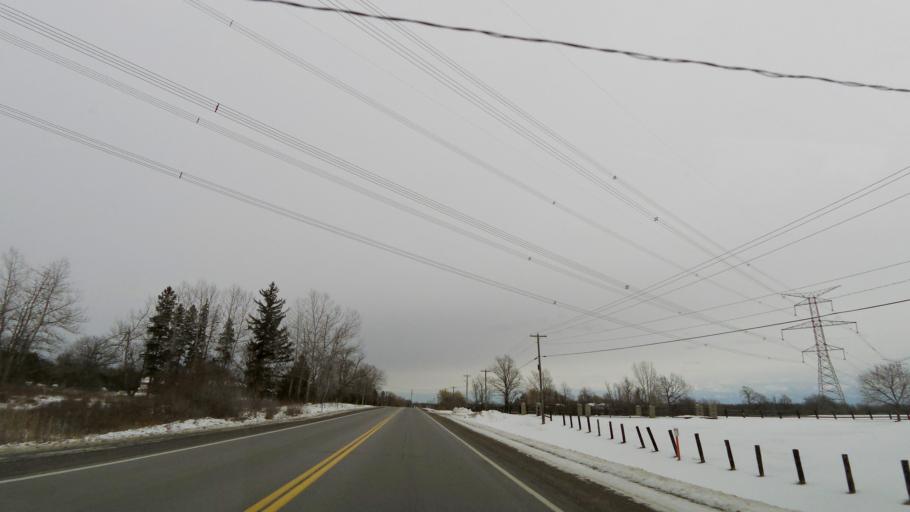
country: CA
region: Ontario
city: Ancaster
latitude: 43.2874
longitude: -80.0872
